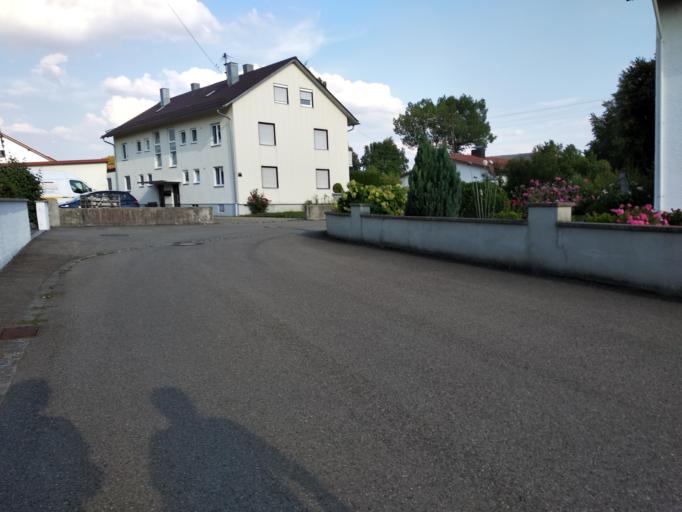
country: DE
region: Bavaria
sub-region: Swabia
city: Westerheim
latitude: 48.0156
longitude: 10.3000
